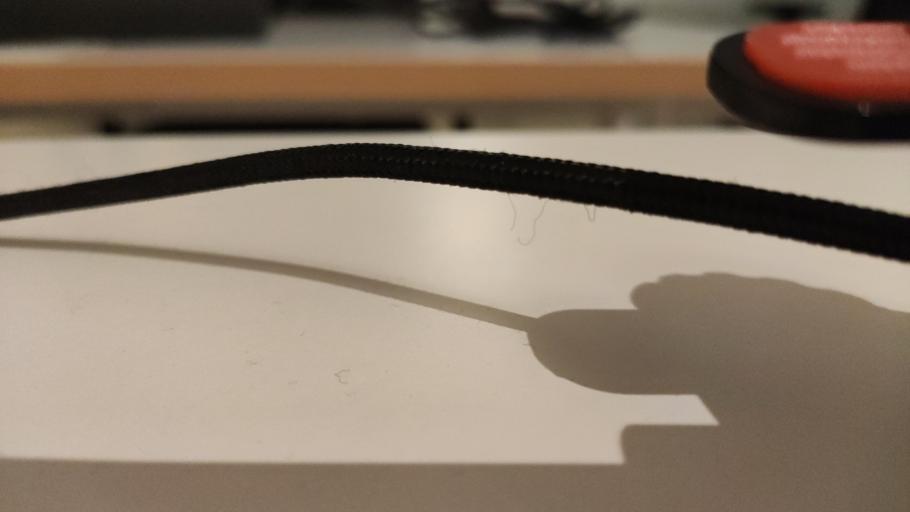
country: RU
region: Moskovskaya
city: Kurovskoye
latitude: 55.5984
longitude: 38.9249
